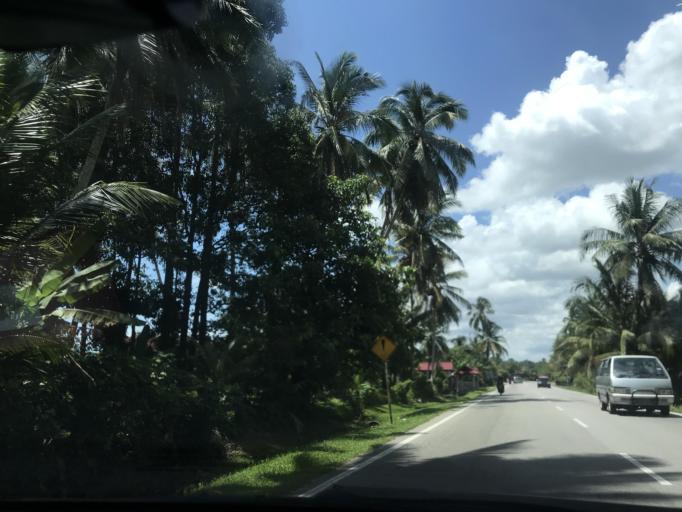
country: MY
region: Kelantan
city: Tumpat
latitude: 6.1940
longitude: 102.1424
